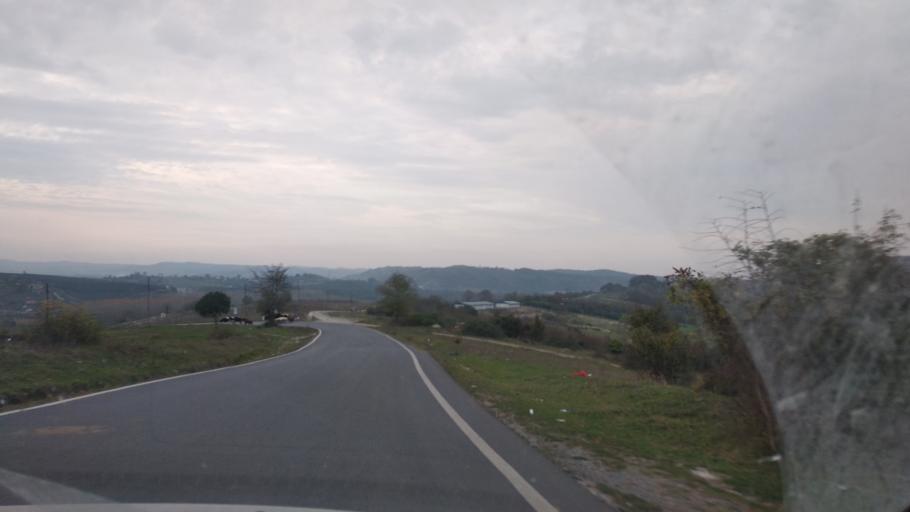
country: TR
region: Sakarya
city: Ortakoy
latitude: 41.0399
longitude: 30.6518
